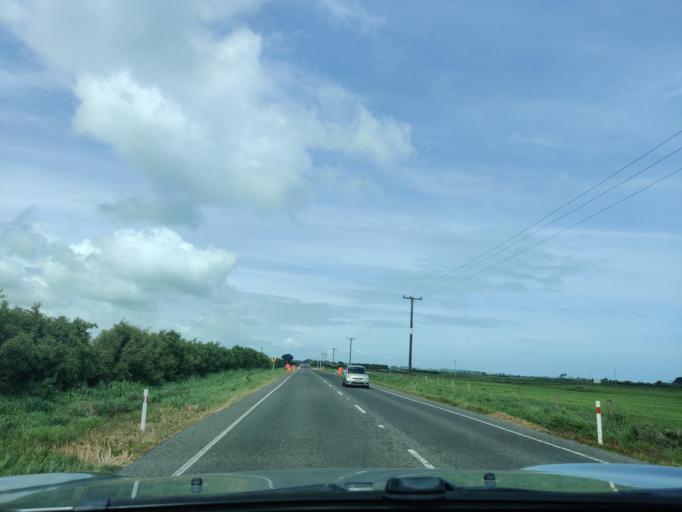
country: NZ
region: Taranaki
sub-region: South Taranaki District
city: Hawera
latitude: -39.5798
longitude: 174.2271
